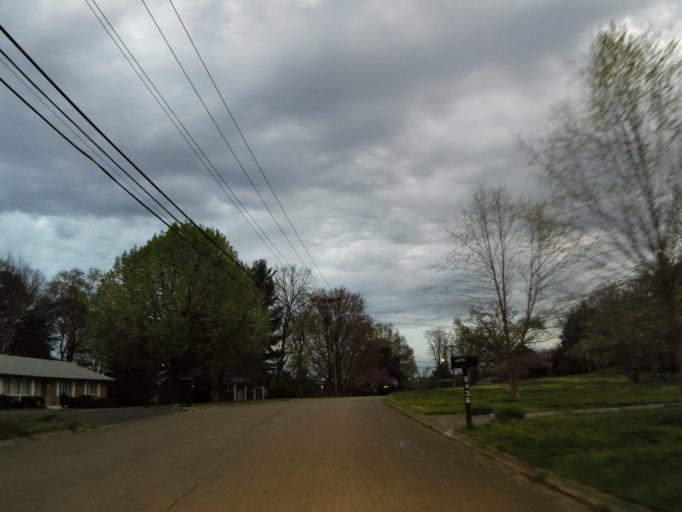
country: US
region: Tennessee
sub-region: Knox County
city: Farragut
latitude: 35.9366
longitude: -84.0539
